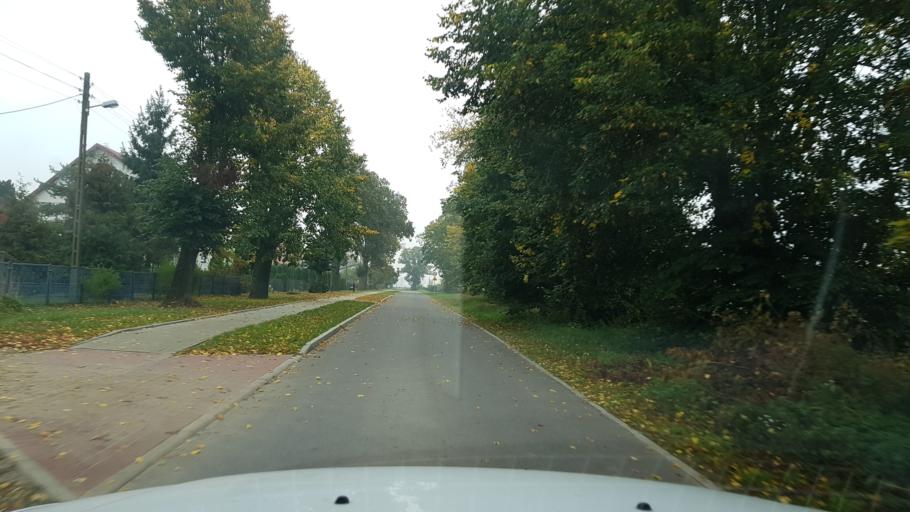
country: PL
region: West Pomeranian Voivodeship
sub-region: Powiat stargardzki
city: Dolice
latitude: 53.1461
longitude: 15.2392
